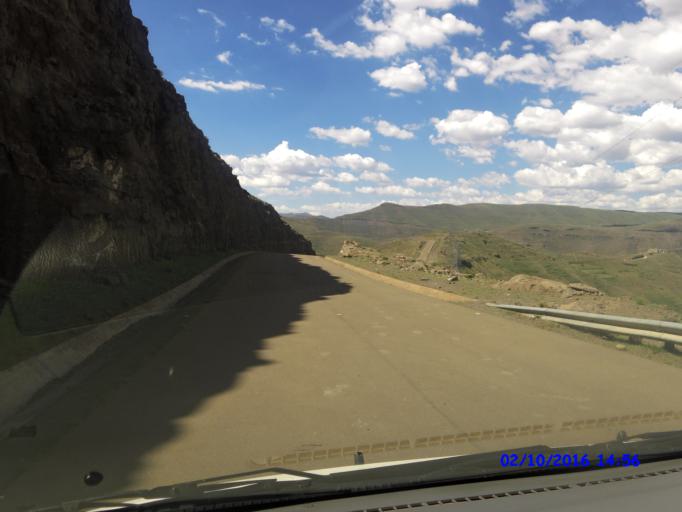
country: LS
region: Maseru
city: Nako
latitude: -29.4679
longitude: 28.0911
